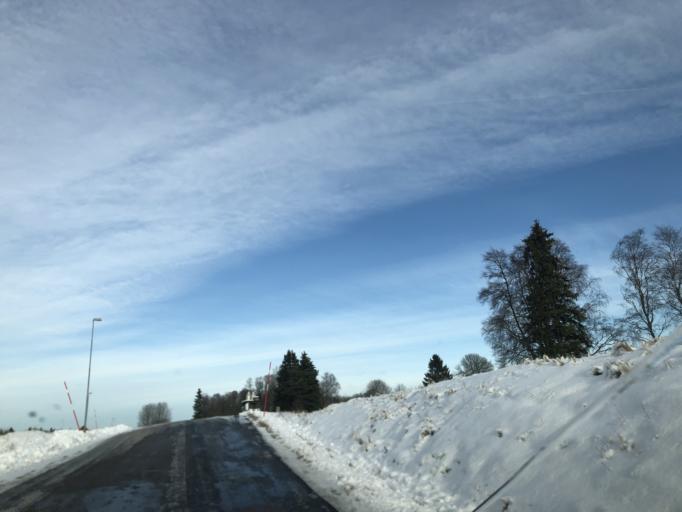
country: SE
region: Vaestra Goetaland
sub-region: Ulricehamns Kommun
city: Ulricehamn
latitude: 57.7928
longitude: 13.5332
